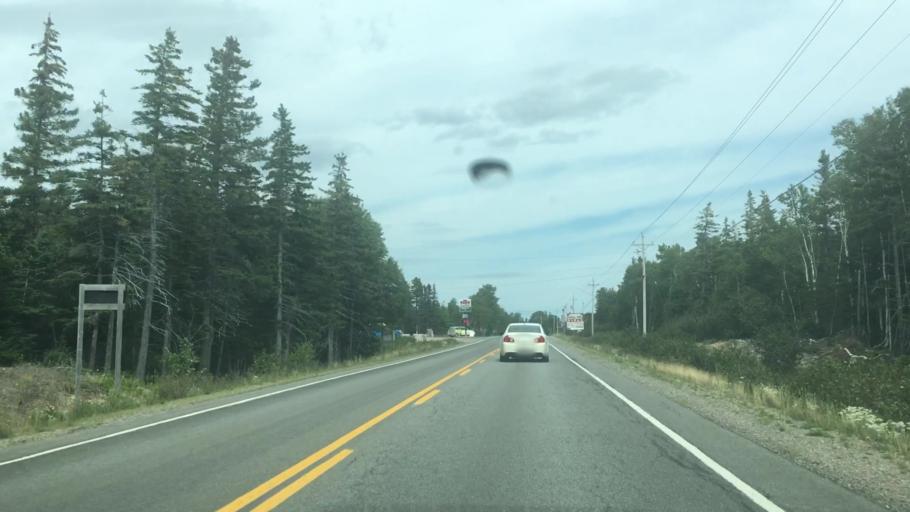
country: CA
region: Nova Scotia
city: Sydney Mines
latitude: 46.5149
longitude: -60.4282
